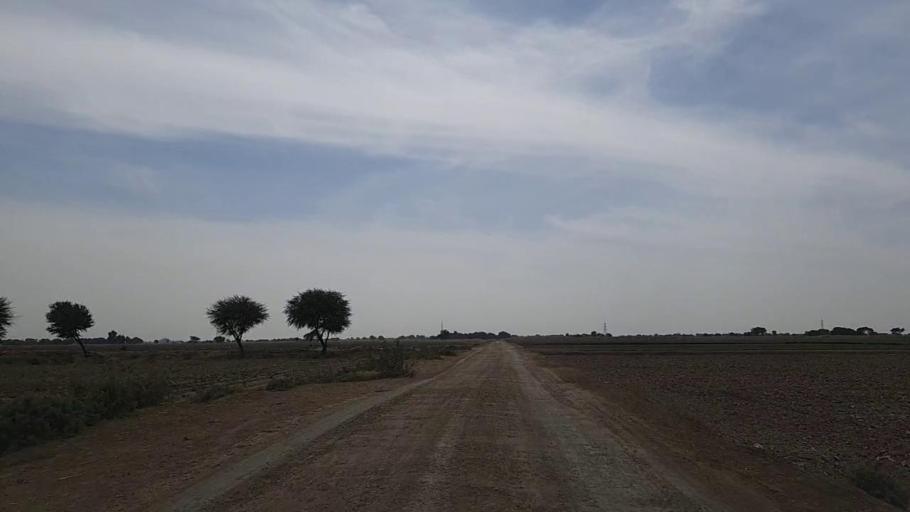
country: PK
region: Sindh
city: Samaro
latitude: 25.3011
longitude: 69.4528
